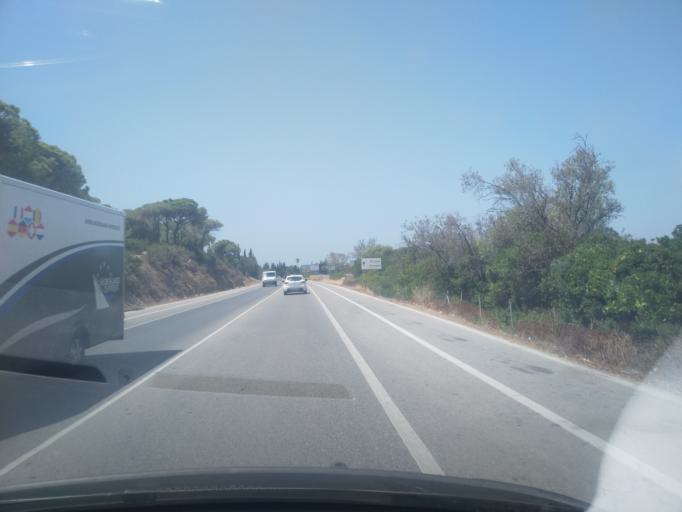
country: ES
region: Andalusia
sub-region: Provincia de Cadiz
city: Chiclana de la Frontera
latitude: 36.3894
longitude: -6.1400
